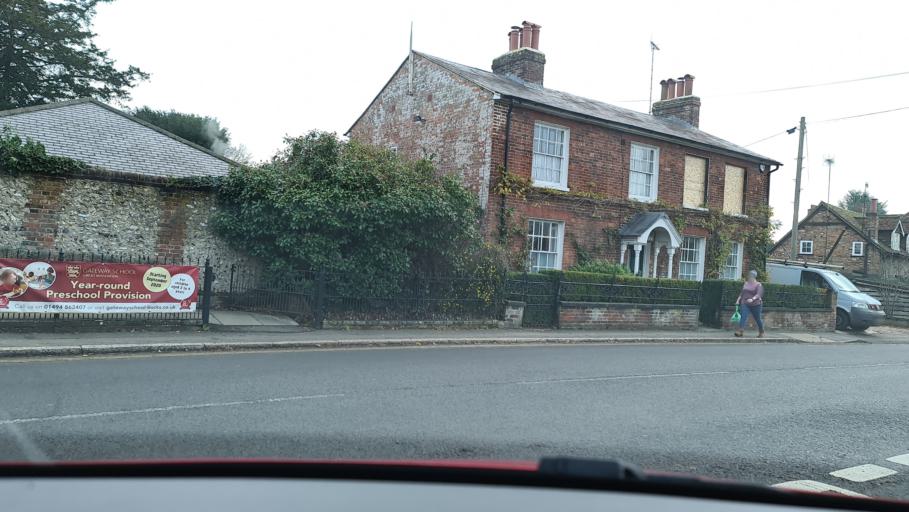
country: GB
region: England
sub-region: Buckinghamshire
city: Great Missenden
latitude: 51.7063
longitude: -0.7099
